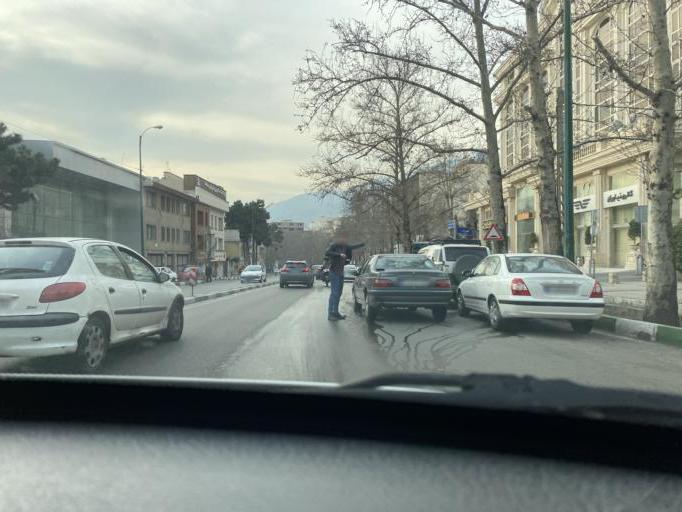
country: IR
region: Tehran
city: Tajrish
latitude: 35.8124
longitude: 51.4569
